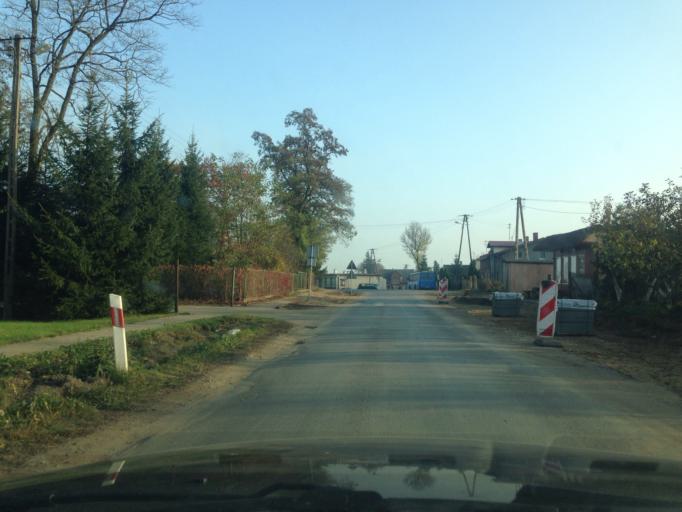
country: PL
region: Kujawsko-Pomorskie
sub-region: Powiat wabrzeski
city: Debowa Laka
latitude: 53.2577
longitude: 19.0950
